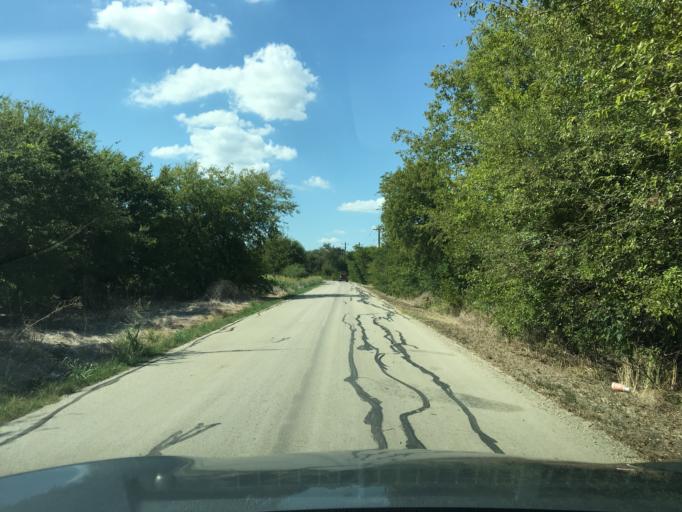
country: US
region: Texas
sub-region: Tarrant County
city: Mansfield
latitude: 32.5248
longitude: -97.0785
